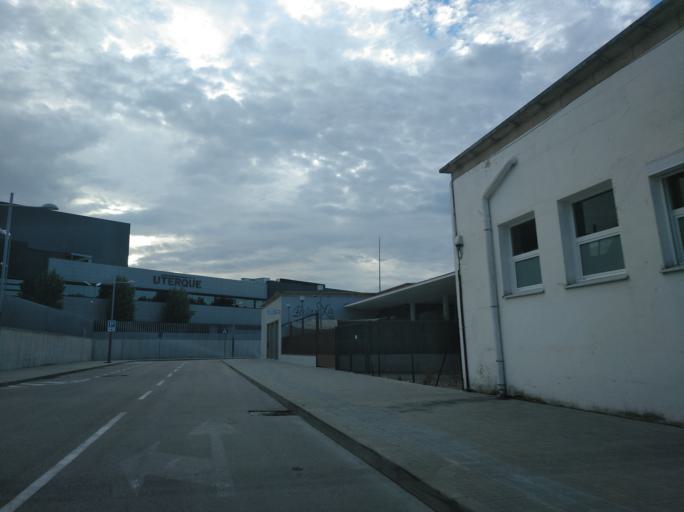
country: ES
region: Catalonia
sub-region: Provincia de Barcelona
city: Tordera
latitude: 41.6953
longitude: 2.7291
